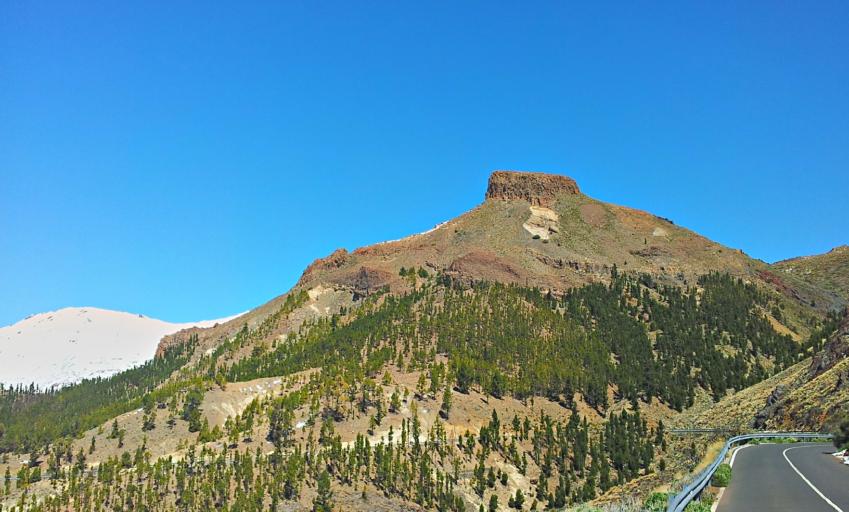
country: ES
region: Canary Islands
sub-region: Provincia de Santa Cruz de Tenerife
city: Vilaflor
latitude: 28.1994
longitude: -16.6733
